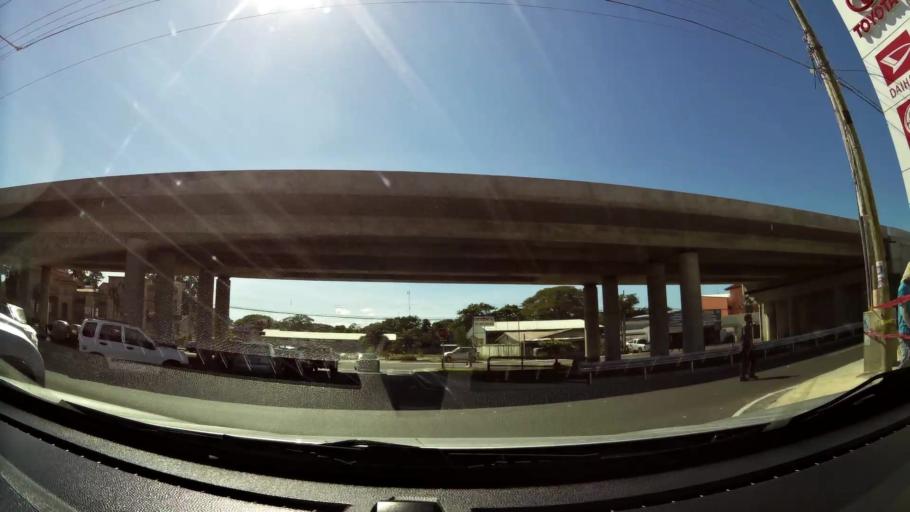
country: CR
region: Guanacaste
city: Liberia
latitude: 10.6275
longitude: -85.4440
